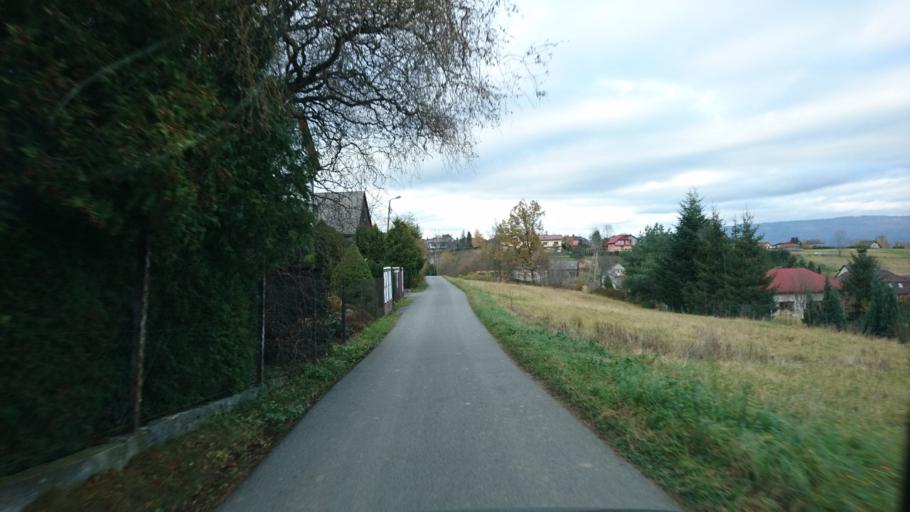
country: PL
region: Silesian Voivodeship
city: Godziszka
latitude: 49.6951
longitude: 19.0728
